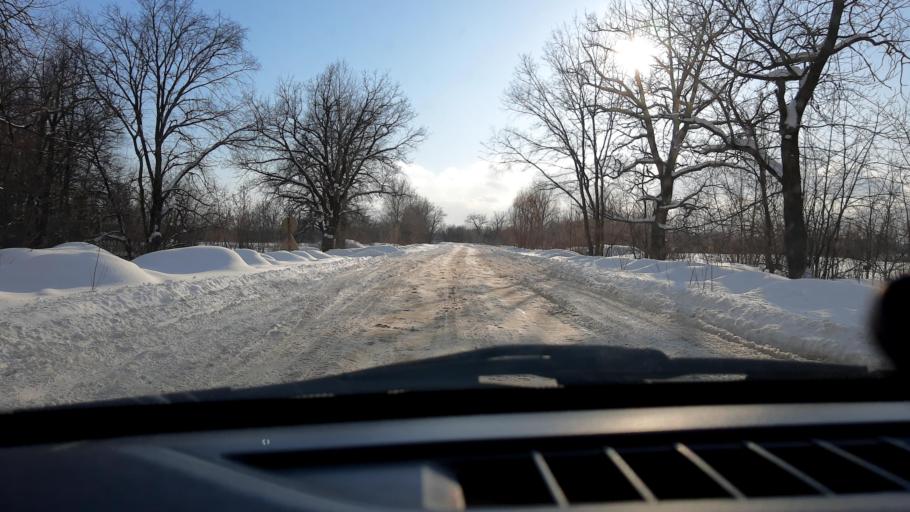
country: RU
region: Bashkortostan
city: Ufa
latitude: 54.6360
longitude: 56.0046
